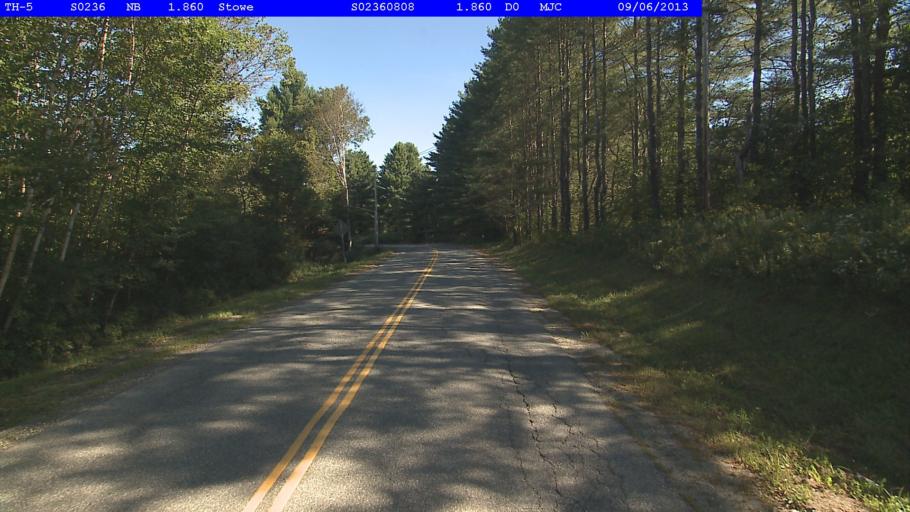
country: US
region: Vermont
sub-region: Washington County
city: Waterbury
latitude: 44.4519
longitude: -72.7293
